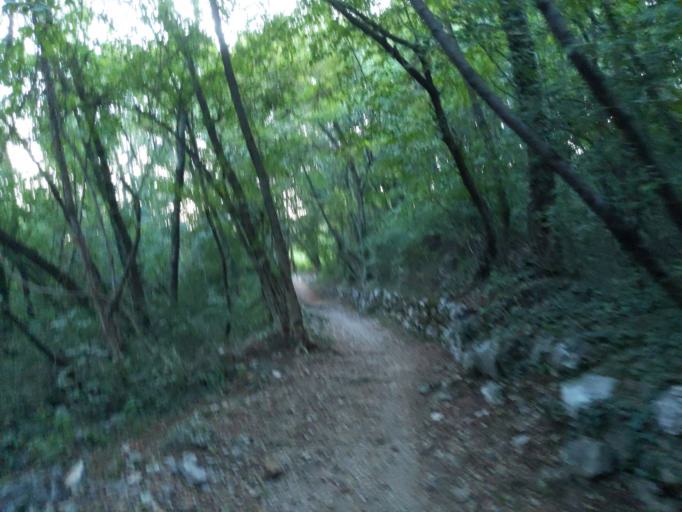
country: CH
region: Ticino
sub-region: Mendrisio District
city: Ligornetto
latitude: 45.8755
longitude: 8.9598
